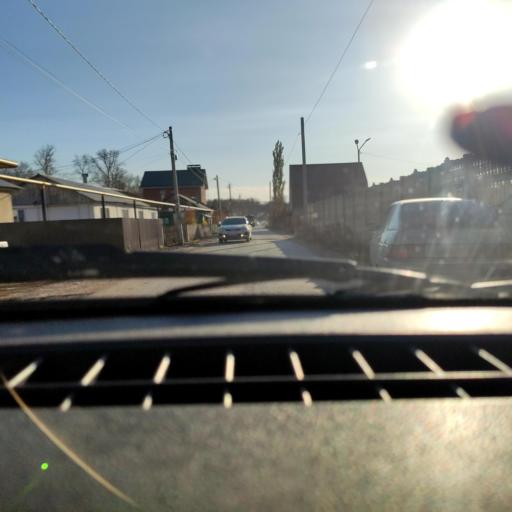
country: RU
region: Bashkortostan
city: Ufa
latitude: 54.6877
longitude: 55.9594
